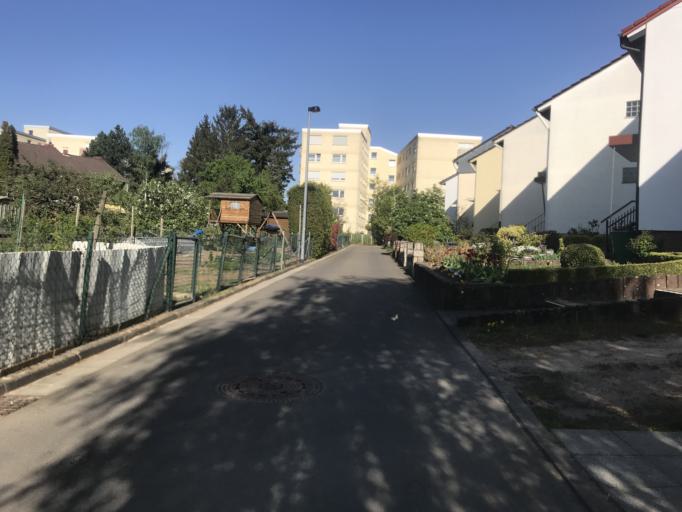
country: DE
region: Rheinland-Pfalz
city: Budenheim
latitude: 50.0181
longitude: 8.1652
